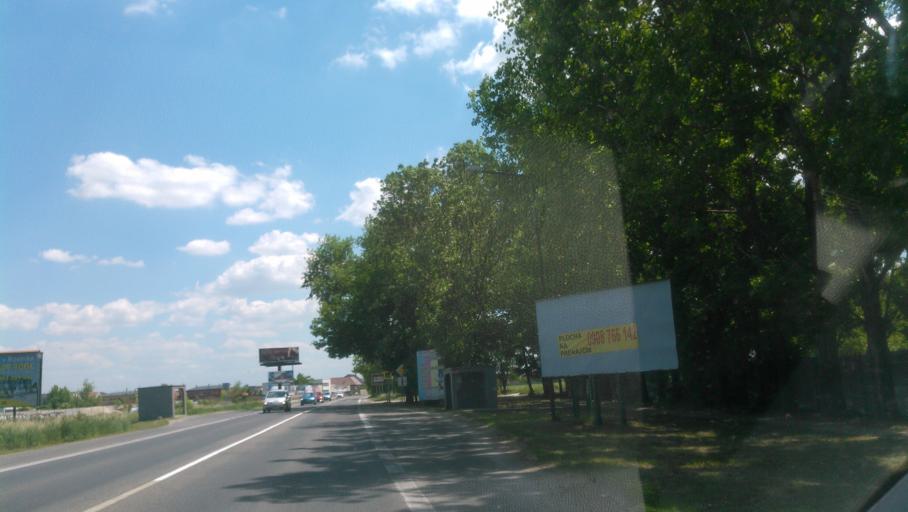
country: SK
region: Bratislavsky
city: Dunajska Luzna
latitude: 48.0924
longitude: 17.2452
